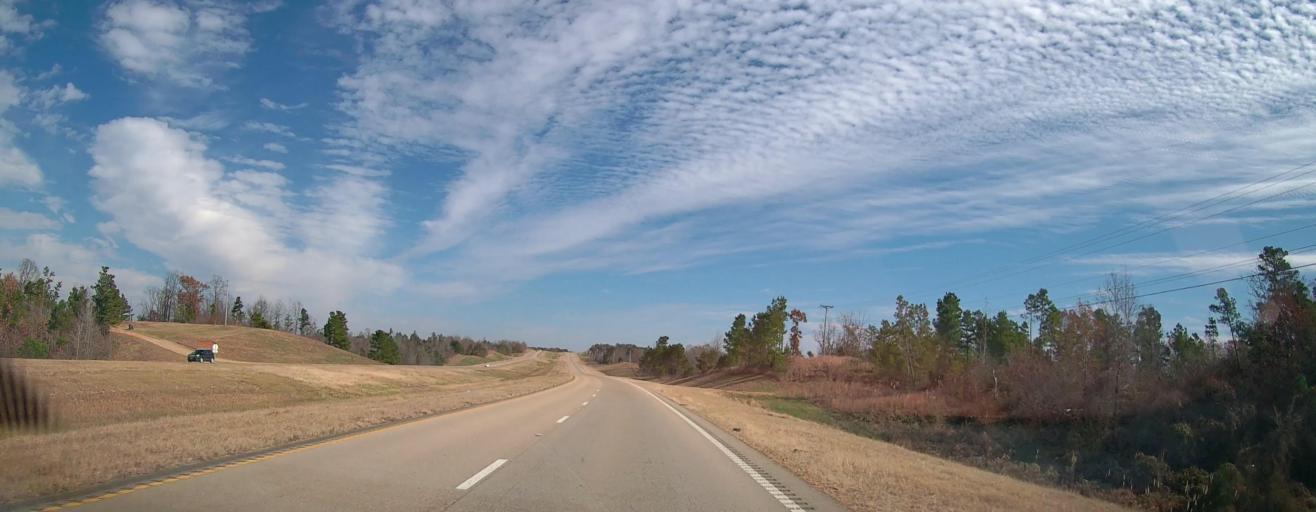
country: US
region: Mississippi
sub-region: Benton County
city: Ashland
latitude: 34.9531
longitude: -89.0049
